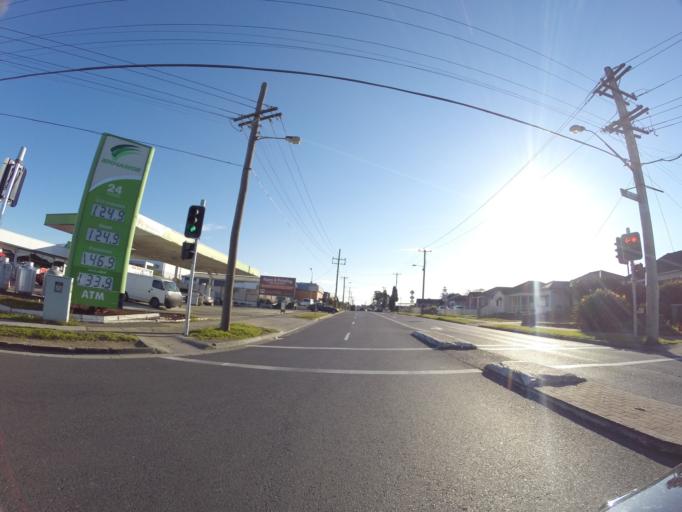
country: AU
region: New South Wales
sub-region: Bankstown
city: Regents Park
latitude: -33.8634
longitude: 151.0090
